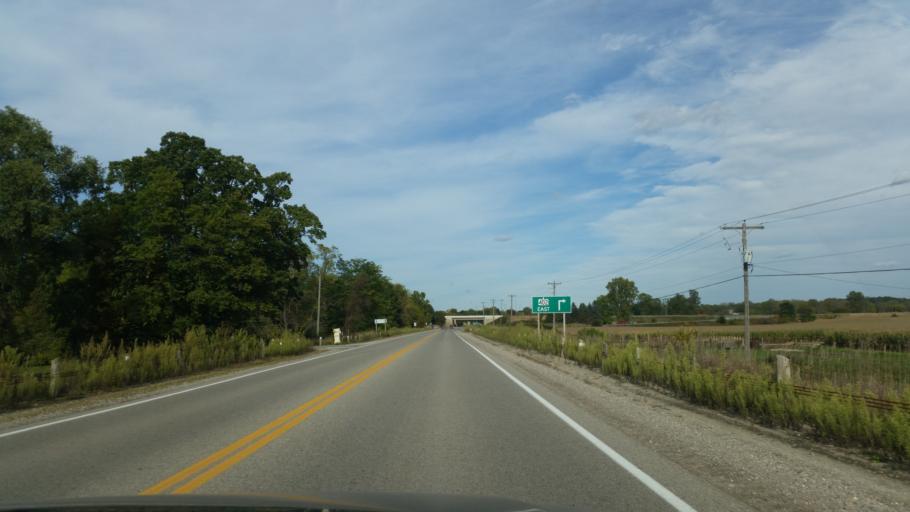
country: CA
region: Ontario
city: Delaware
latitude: 42.8967
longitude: -81.4374
